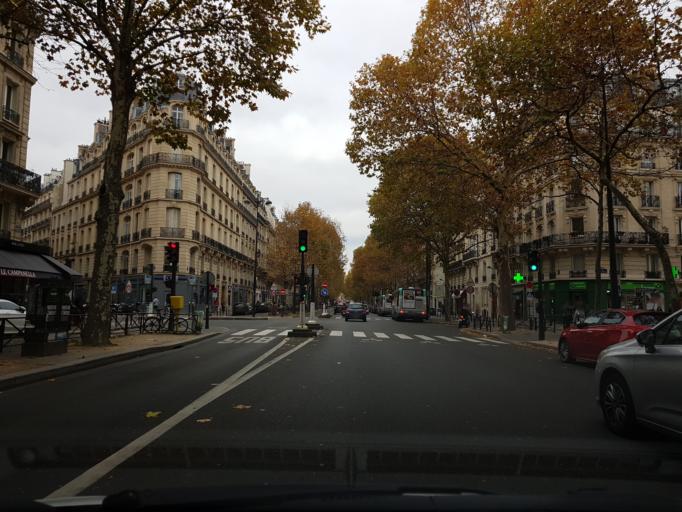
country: FR
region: Ile-de-France
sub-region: Departement des Hauts-de-Seine
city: Vanves
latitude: 48.8585
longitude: 2.3036
